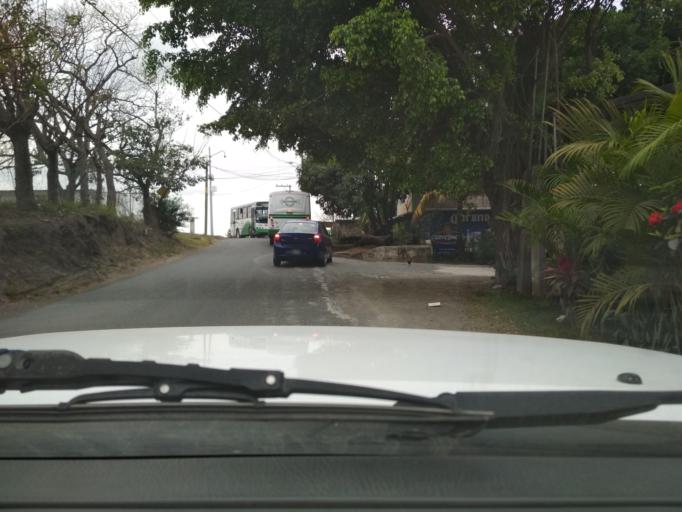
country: MX
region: Veracruz
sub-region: Medellin
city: Fraccionamiento Arboledas San Ramon
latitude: 19.0900
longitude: -96.1288
